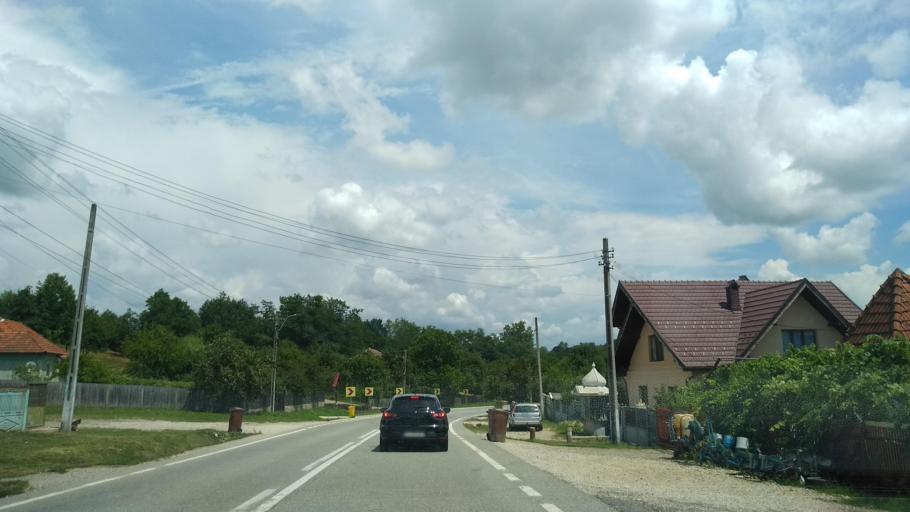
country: RO
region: Gorj
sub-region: Comuna Bengesti-Ciocadia
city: Balcesti
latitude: 45.1161
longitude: 23.6631
